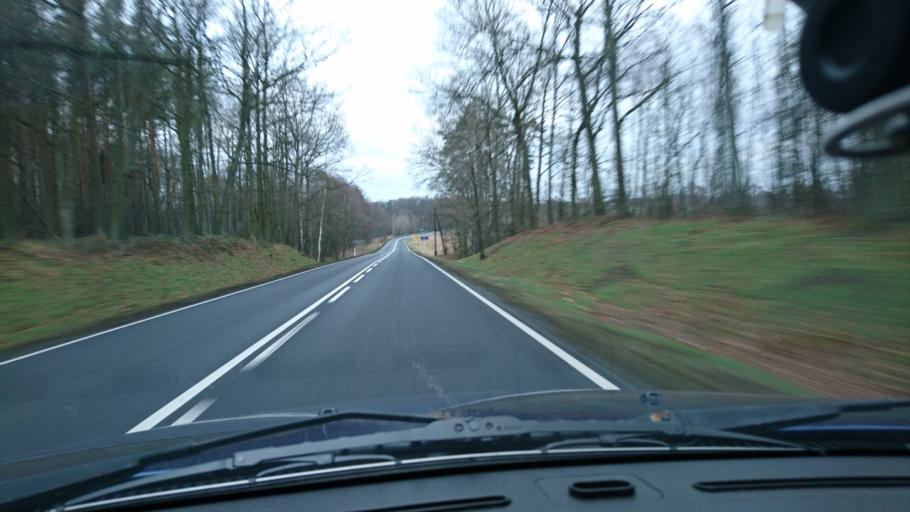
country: PL
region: Opole Voivodeship
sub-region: Powiat kluczborski
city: Kluczbork
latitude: 50.9518
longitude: 18.3114
